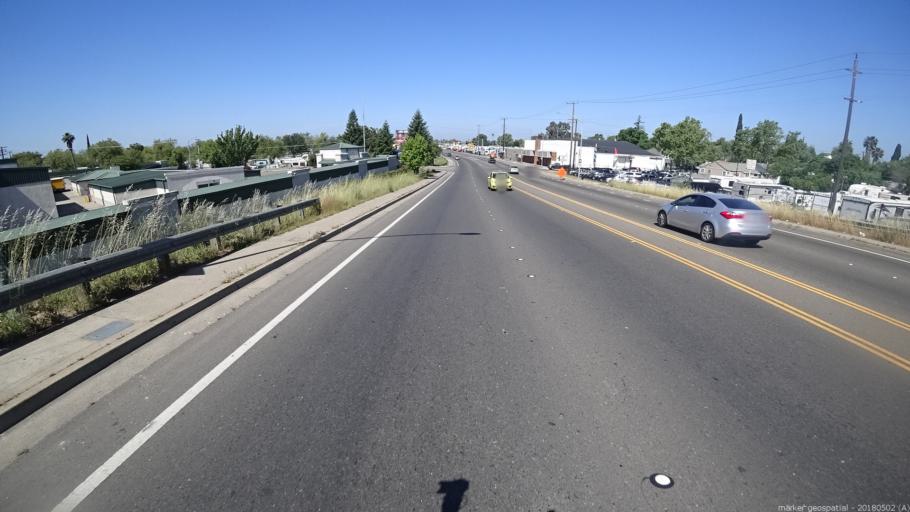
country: US
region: California
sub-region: Sacramento County
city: Arden-Arcade
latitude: 38.6109
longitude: -121.4369
